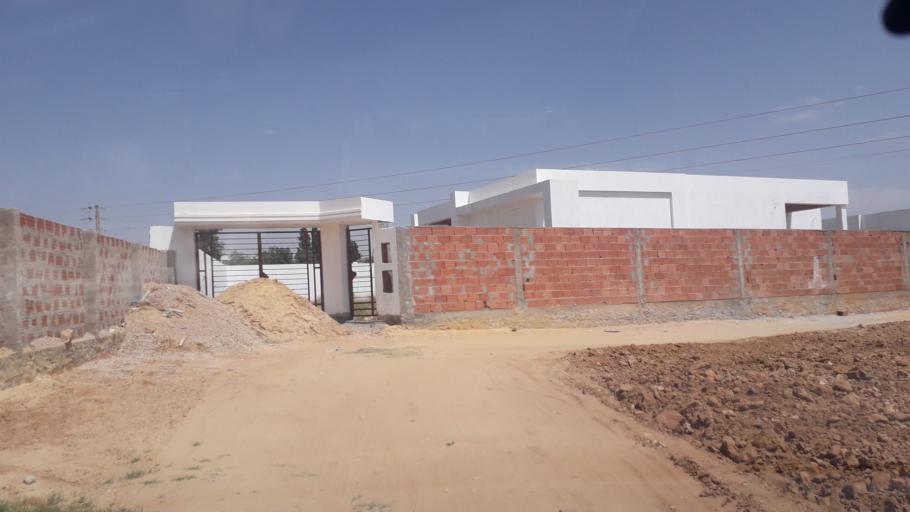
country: TN
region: Safaqis
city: Al Qarmadah
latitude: 34.8345
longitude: 10.7663
